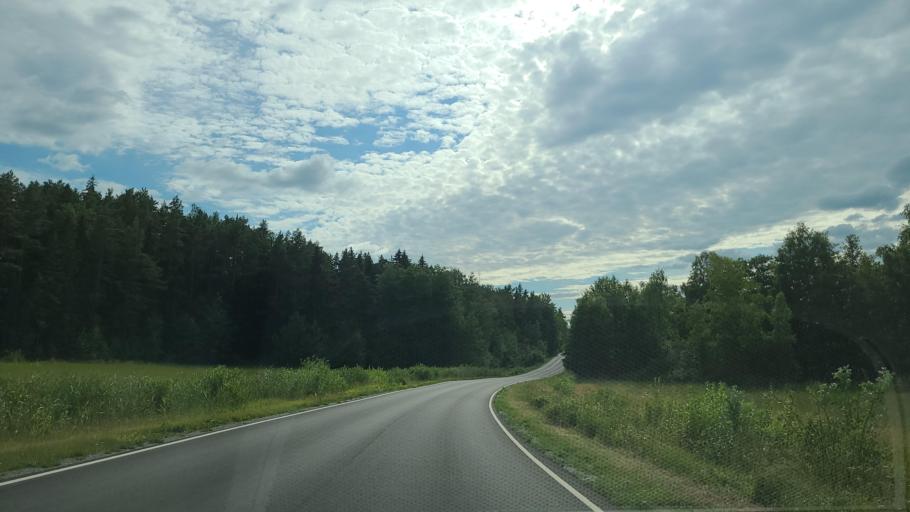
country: FI
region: Varsinais-Suomi
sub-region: Turku
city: Rymaettylae
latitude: 60.3320
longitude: 21.9782
